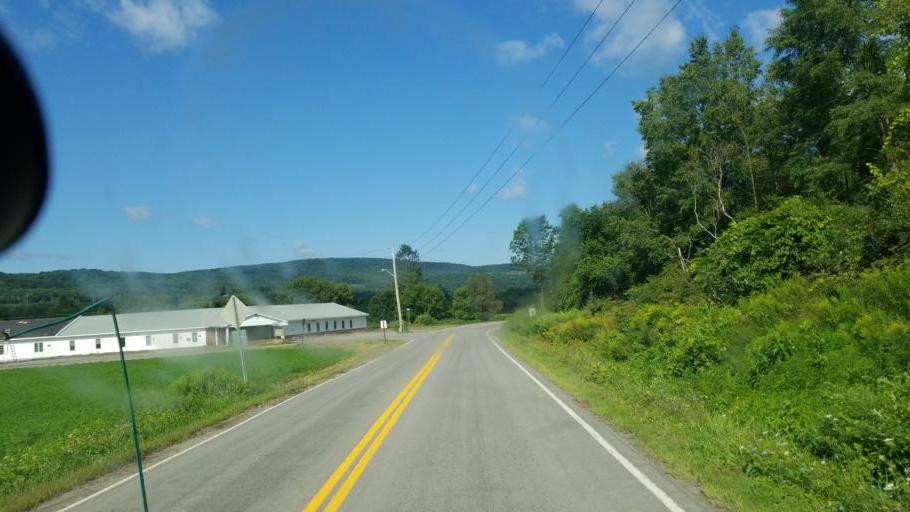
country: US
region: New York
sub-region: Steuben County
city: Canisteo
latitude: 42.2927
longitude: -77.6209
